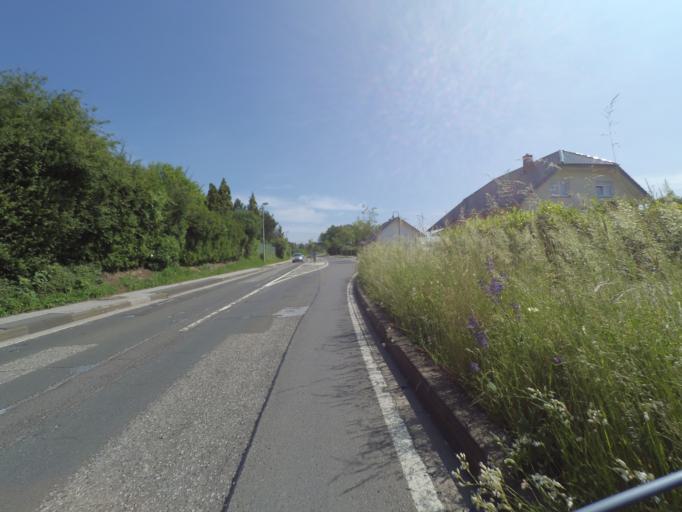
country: DE
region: Rheinland-Pfalz
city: Ney
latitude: 50.2099
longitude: 7.5354
